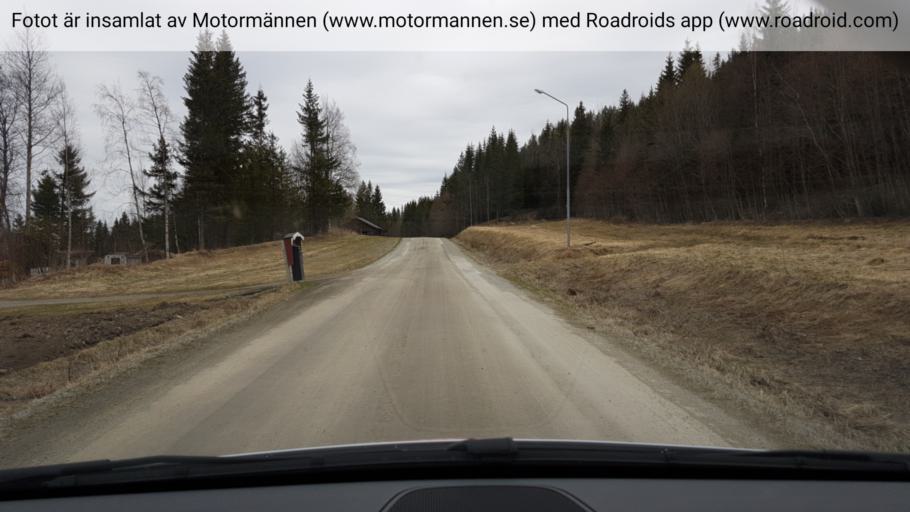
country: SE
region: Jaemtland
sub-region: Bergs Kommun
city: Hoverberg
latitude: 62.9320
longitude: 14.2875
